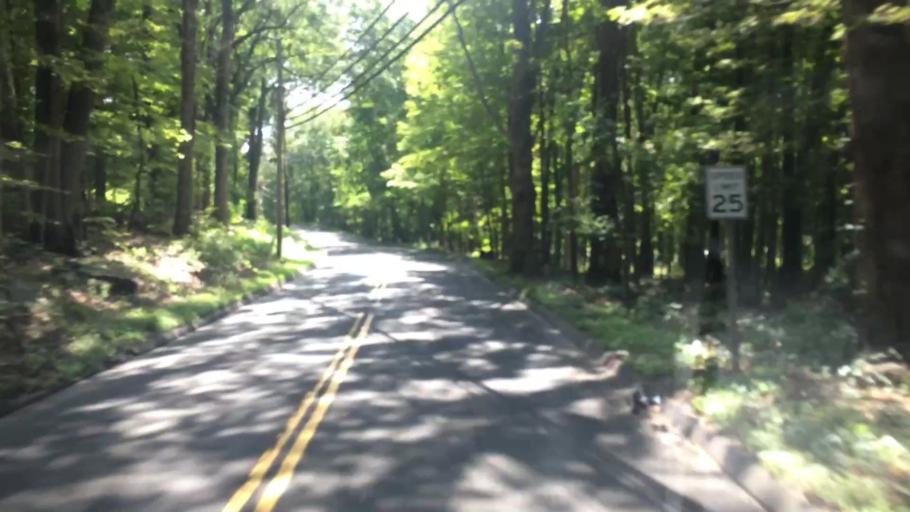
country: US
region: Connecticut
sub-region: Fairfield County
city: Danbury
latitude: 41.4053
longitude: -73.4777
